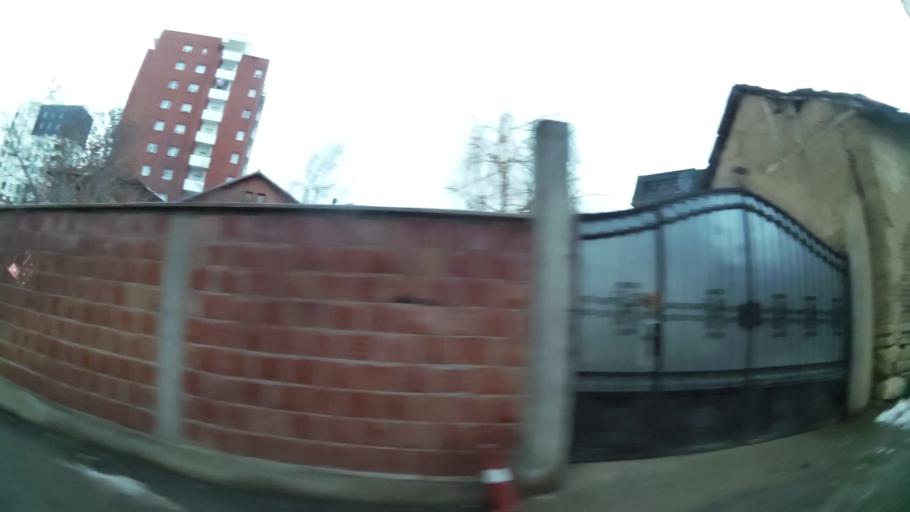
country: XK
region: Pristina
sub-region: Komuna e Prishtines
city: Pristina
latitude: 42.6580
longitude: 21.1718
